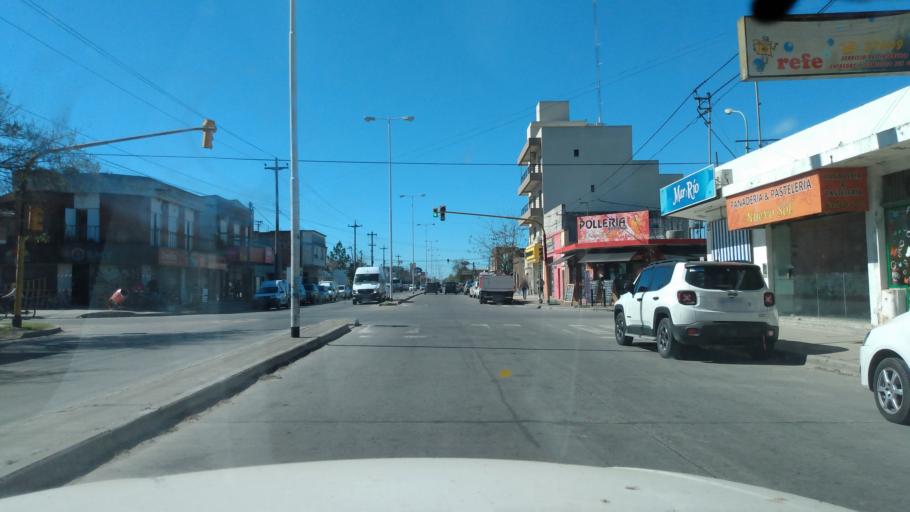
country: AR
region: Buenos Aires
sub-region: Partido de Lujan
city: Lujan
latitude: -34.5604
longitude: -59.1098
